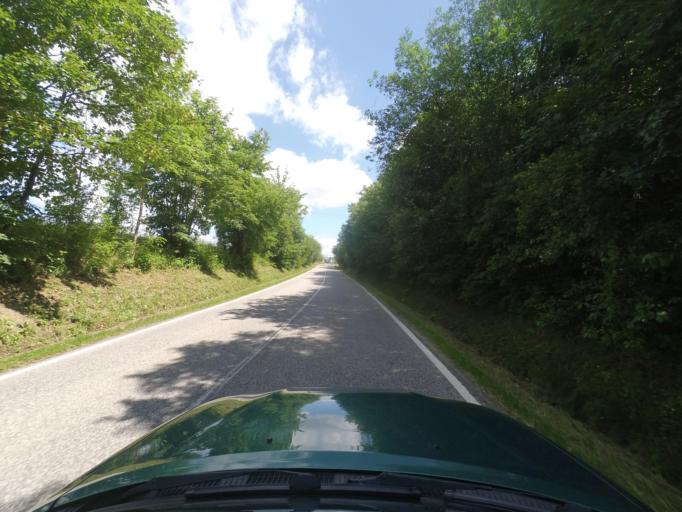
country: CZ
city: Dobruska
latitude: 50.3093
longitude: 16.1878
